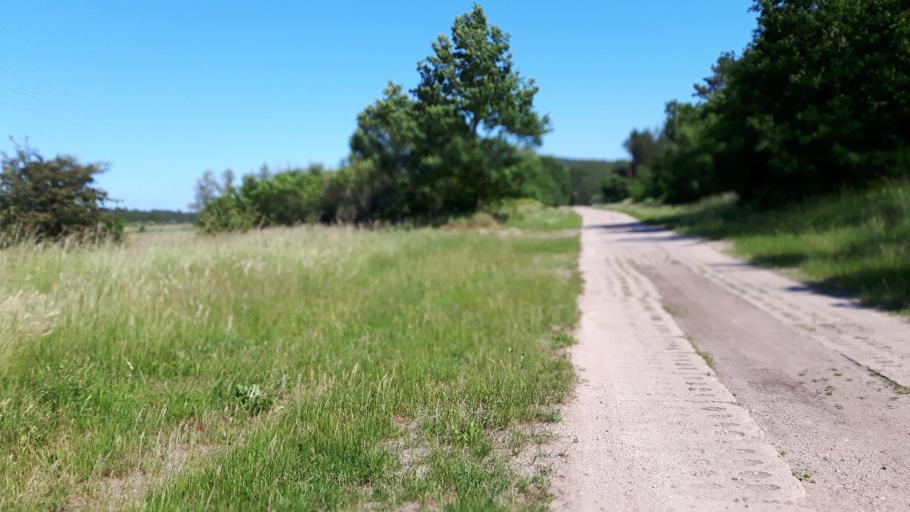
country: PL
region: Pomeranian Voivodeship
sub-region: Powiat slupski
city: Glowczyce
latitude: 54.6418
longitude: 17.4004
